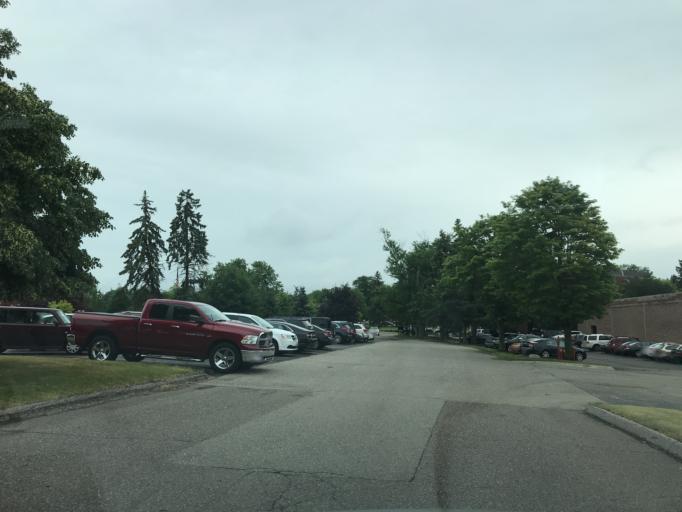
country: US
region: Michigan
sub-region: Oakland County
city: Farmington
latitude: 42.4710
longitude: -83.3889
